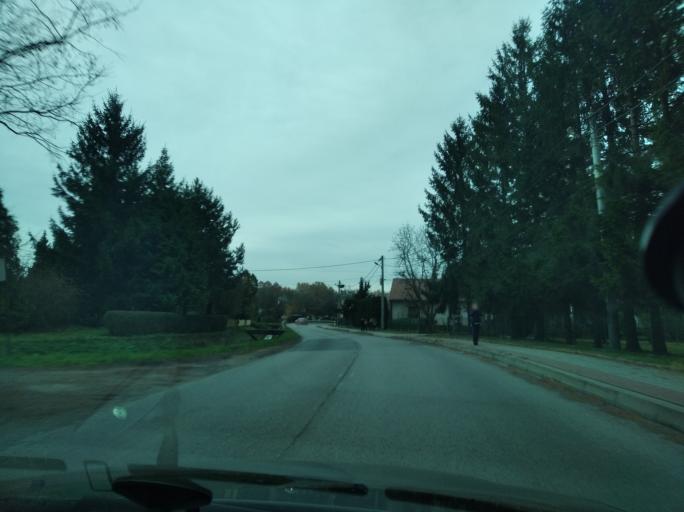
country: PL
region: Subcarpathian Voivodeship
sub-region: Powiat lancucki
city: Krzemienica
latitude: 50.0797
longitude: 22.1899
